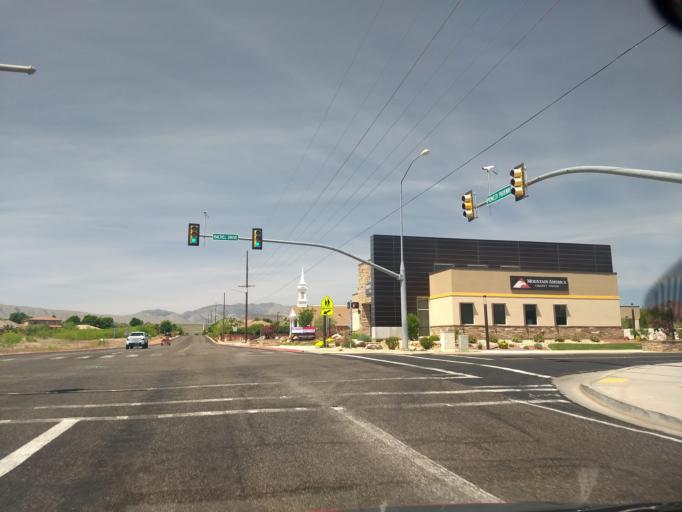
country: US
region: Utah
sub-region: Washington County
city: Santa Clara
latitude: 37.1466
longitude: -113.6607
